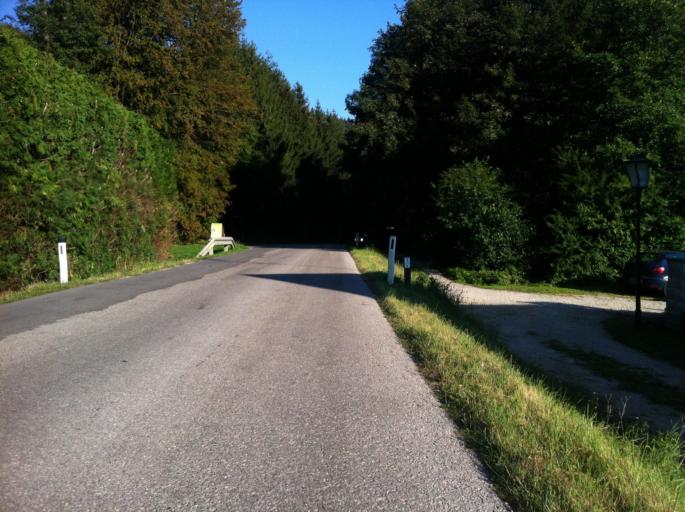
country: AT
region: Lower Austria
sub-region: Politischer Bezirk Wien-Umgebung
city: Pressbaum
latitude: 48.1990
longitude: 16.1155
